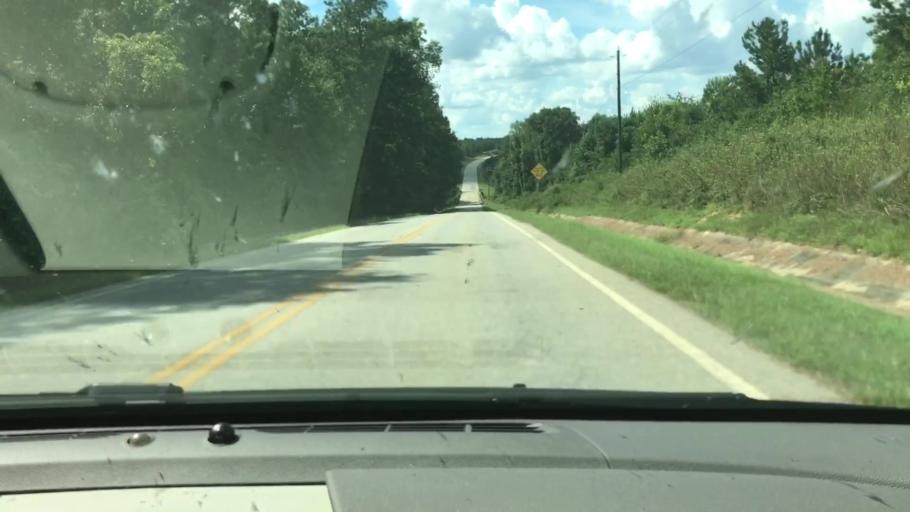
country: US
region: Georgia
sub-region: Quitman County
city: Georgetown
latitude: 31.7635
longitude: -85.0811
